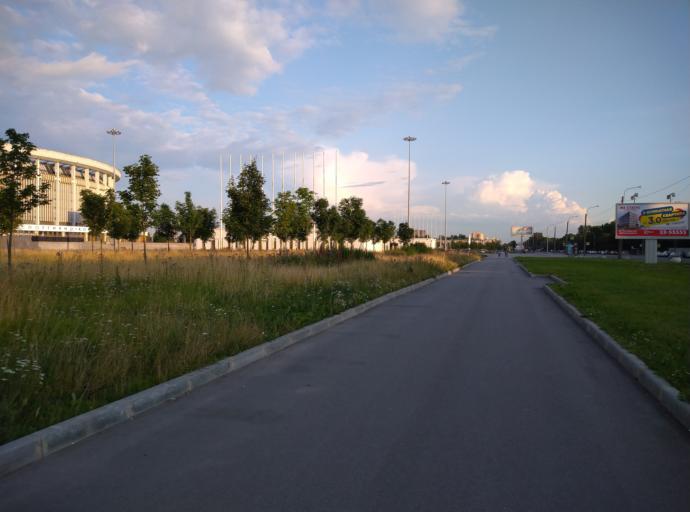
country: RU
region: St.-Petersburg
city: Kupchino
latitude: 59.8708
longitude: 30.3372
